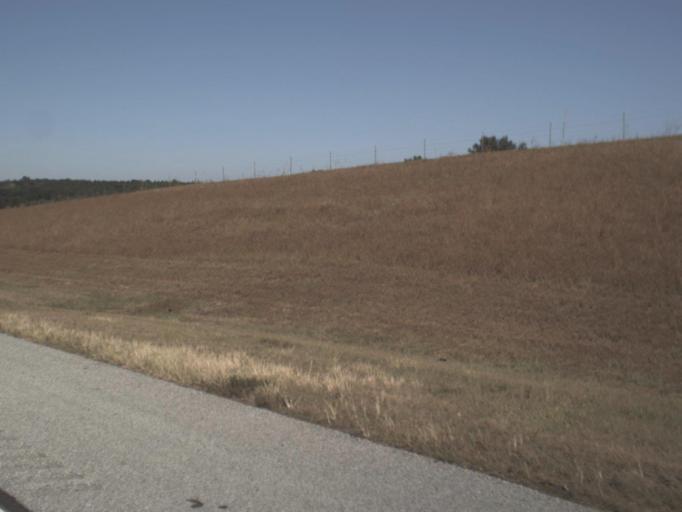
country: US
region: Florida
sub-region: Lake County
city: Minneola
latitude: 28.6177
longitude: -81.7425
